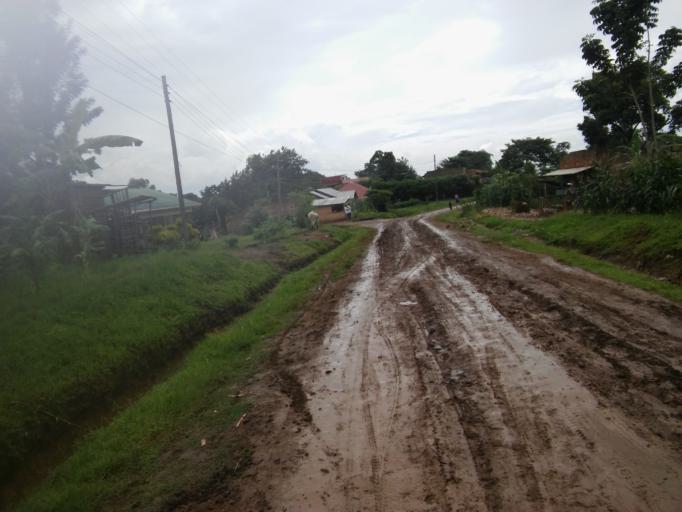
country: UG
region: Eastern Region
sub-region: Mbale District
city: Mbale
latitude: 1.0326
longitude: 34.1978
